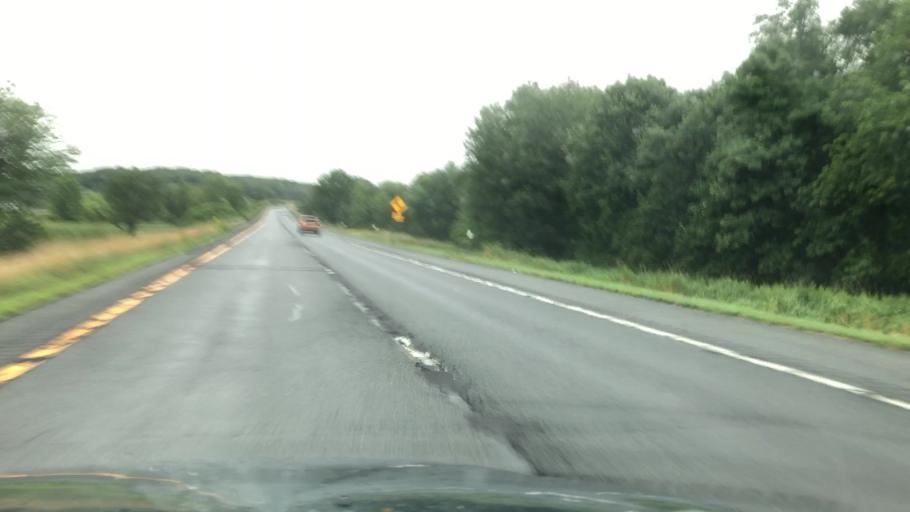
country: US
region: New York
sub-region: Orange County
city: Otisville
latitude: 41.3881
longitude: -74.5709
